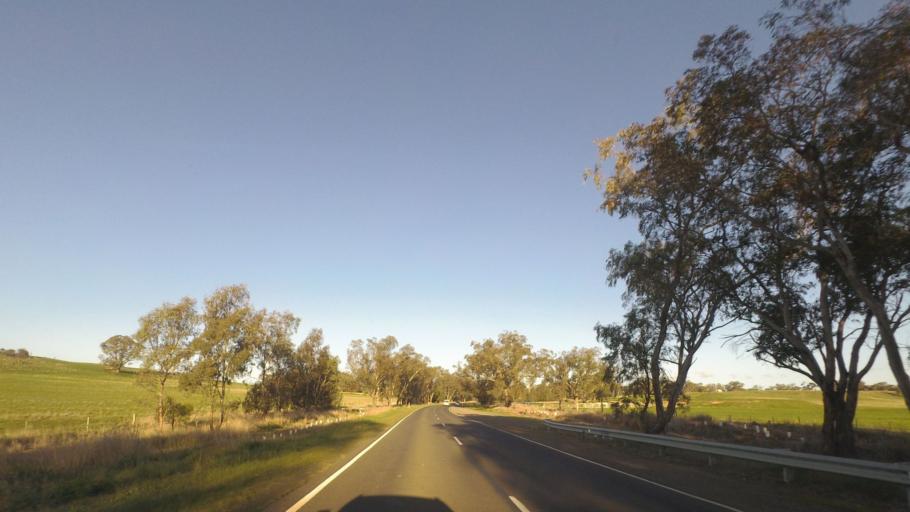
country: AU
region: Victoria
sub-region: Mount Alexander
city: Castlemaine
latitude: -37.0947
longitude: 144.5097
